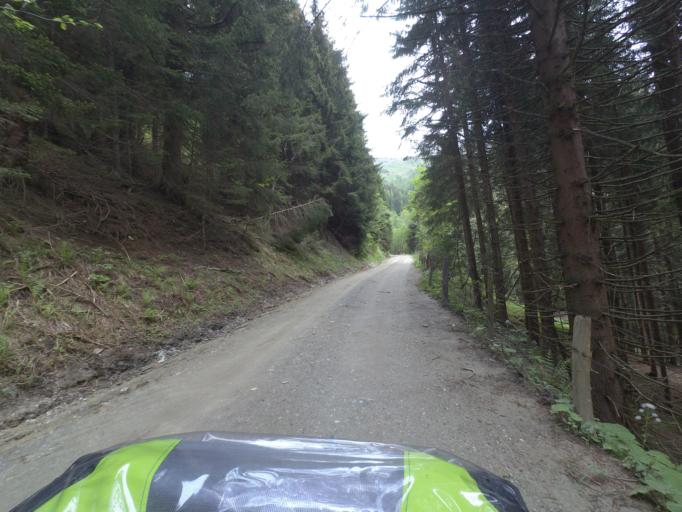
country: AT
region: Salzburg
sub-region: Politischer Bezirk Sankt Johann im Pongau
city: Dorfgastein
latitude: 47.2567
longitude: 13.1248
